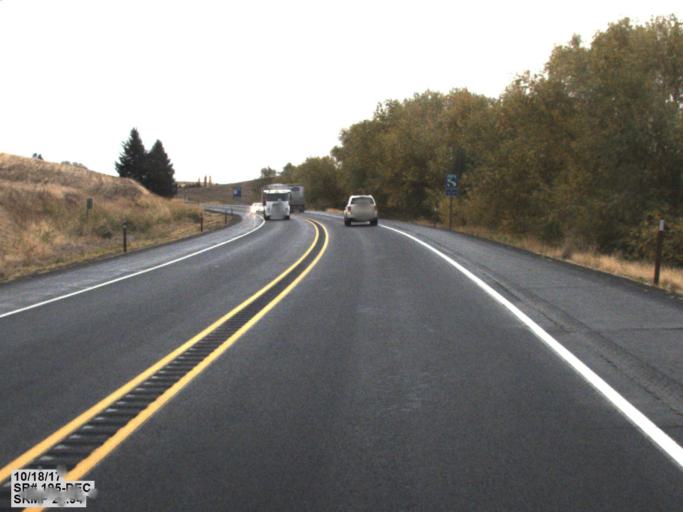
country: US
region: Washington
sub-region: Whitman County
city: Pullman
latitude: 46.7426
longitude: -117.2330
